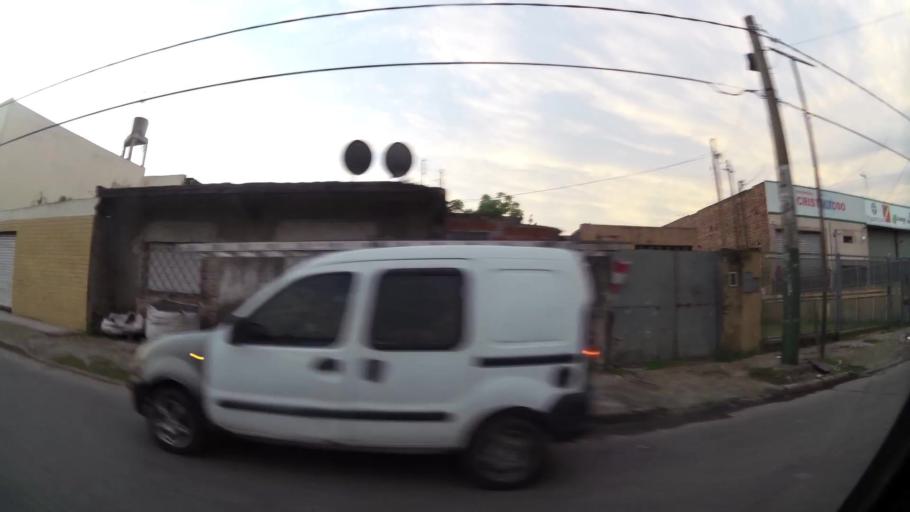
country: AR
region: Buenos Aires
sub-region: Partido de Lomas de Zamora
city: Lomas de Zamora
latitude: -34.7518
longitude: -58.3682
